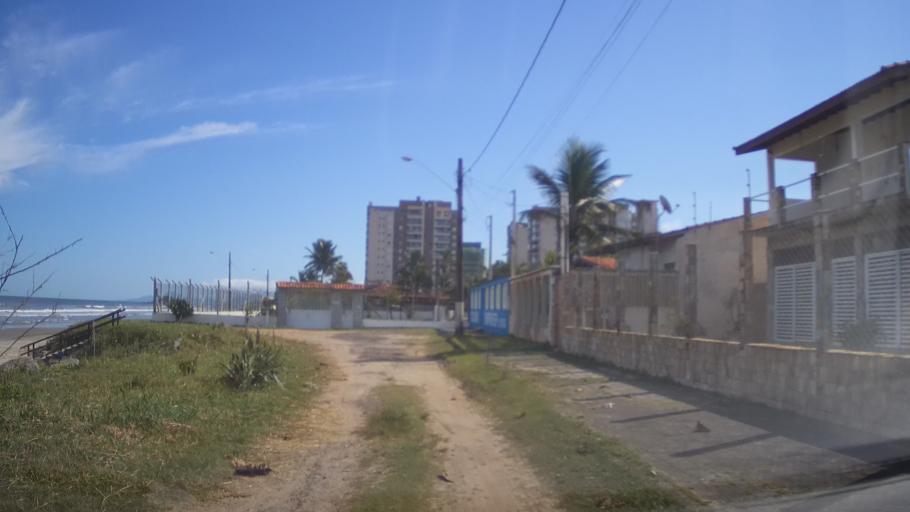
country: BR
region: Sao Paulo
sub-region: Itanhaem
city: Itanhaem
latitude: -24.1803
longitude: -46.7763
